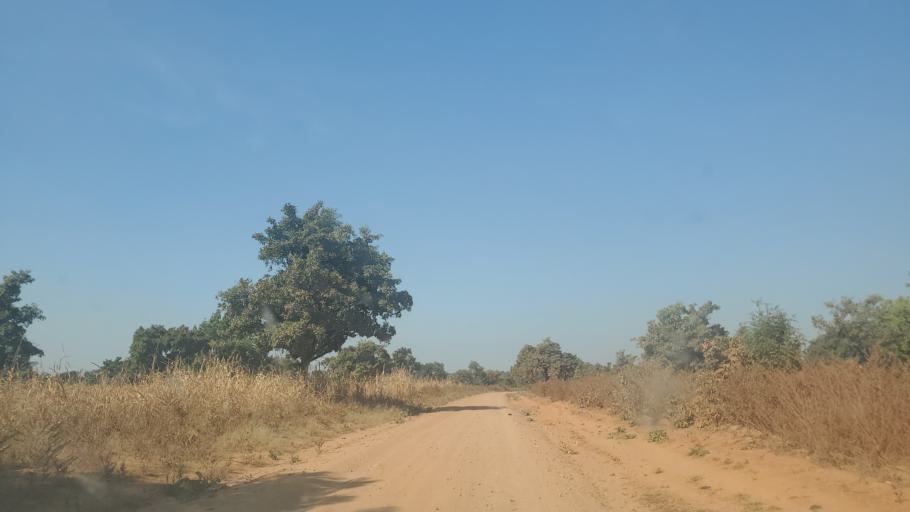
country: NG
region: Niger
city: Badeggi
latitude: 9.1211
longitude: 6.1928
